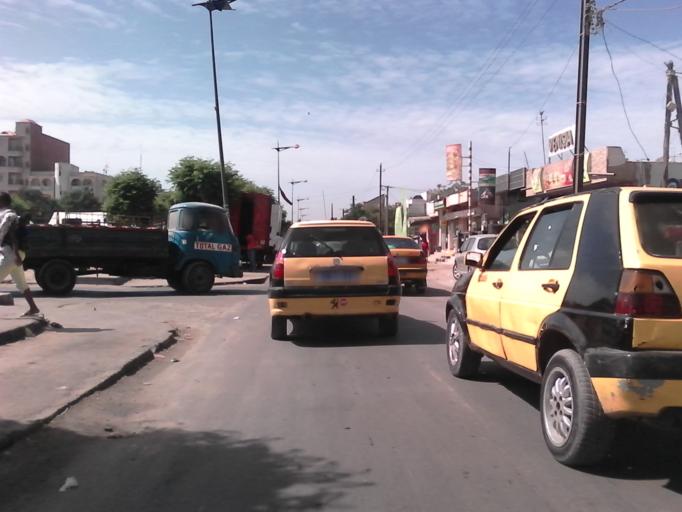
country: SN
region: Dakar
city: Grand Dakar
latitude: 14.7090
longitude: -17.4534
